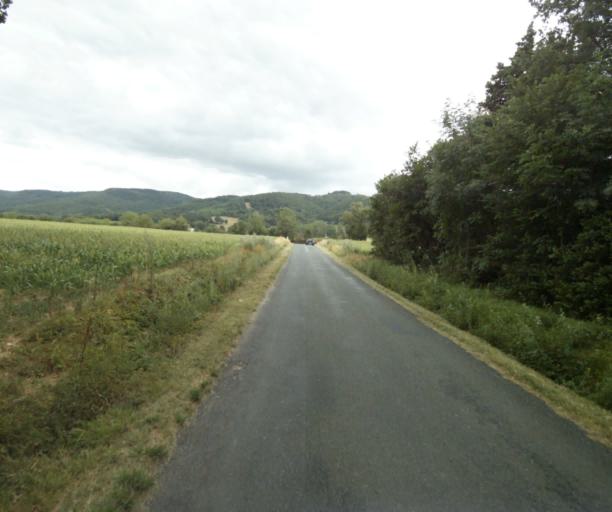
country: FR
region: Midi-Pyrenees
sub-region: Departement du Tarn
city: Soreze
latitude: 43.4650
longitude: 2.0845
